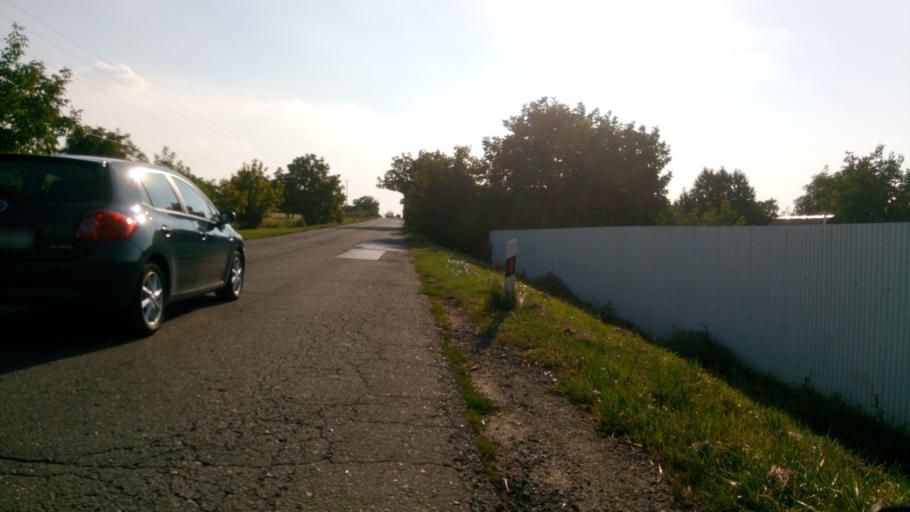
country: HU
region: Pest
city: Budaors
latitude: 47.4464
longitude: 18.9559
